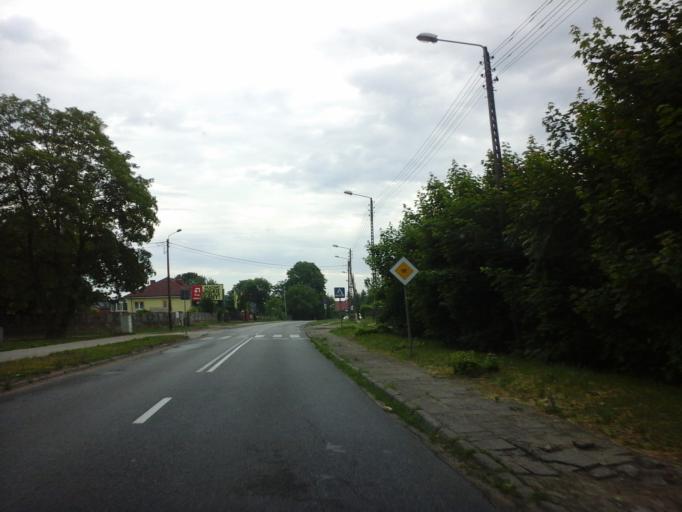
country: PL
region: West Pomeranian Voivodeship
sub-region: Powiat choszczenski
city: Choszczno
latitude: 53.1675
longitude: 15.4351
